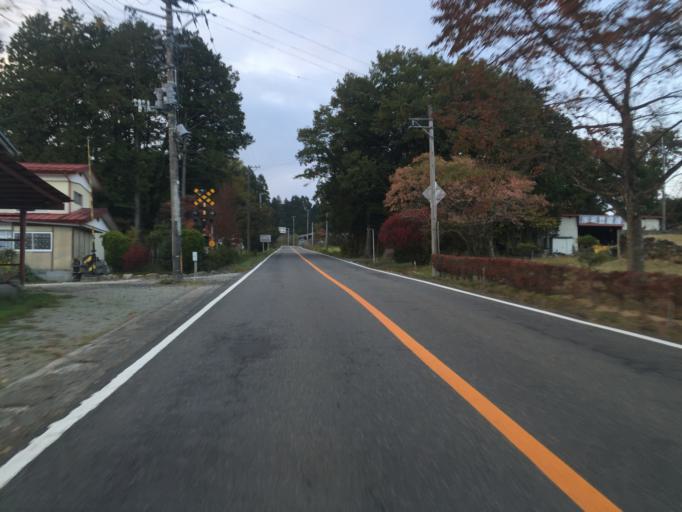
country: JP
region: Fukushima
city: Nihommatsu
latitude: 37.6224
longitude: 140.3598
